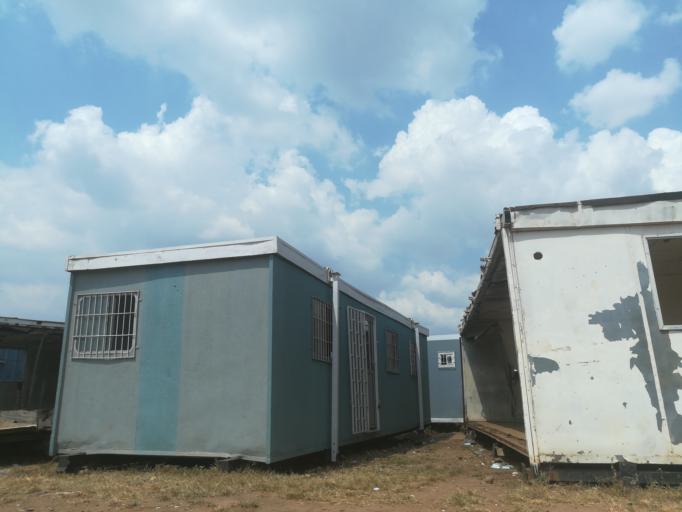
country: NG
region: Abuja Federal Capital Territory
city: Abuja
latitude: 9.0594
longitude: 7.4474
